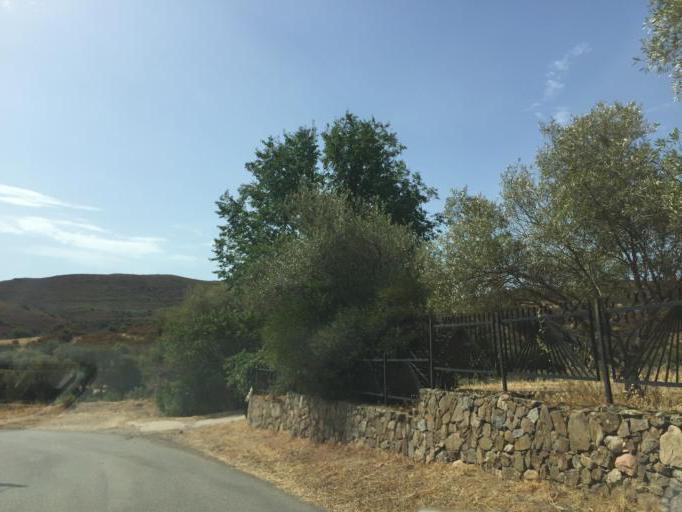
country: IT
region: Sardinia
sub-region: Provincia di Olbia-Tempio
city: San Teodoro
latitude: 40.7233
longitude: 9.6388
